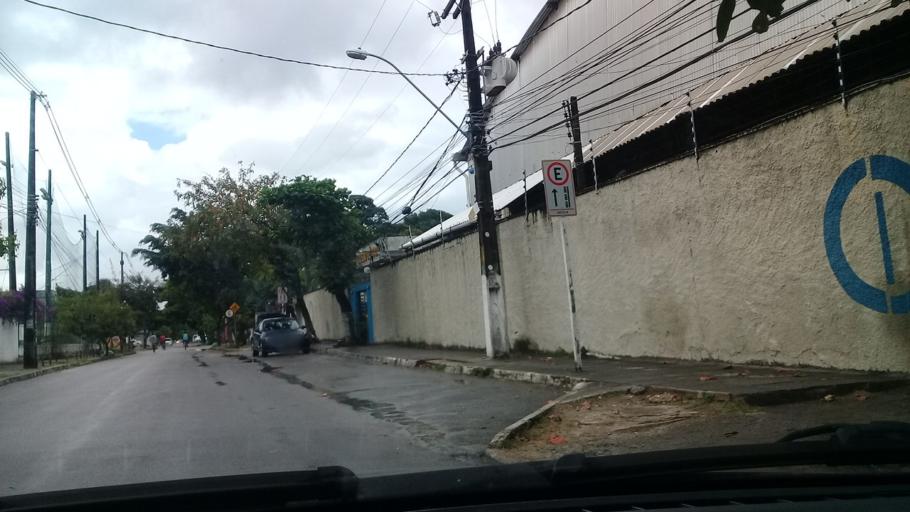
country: BR
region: Pernambuco
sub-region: Jaboatao Dos Guararapes
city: Jaboatao
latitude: -8.1441
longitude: -34.9157
